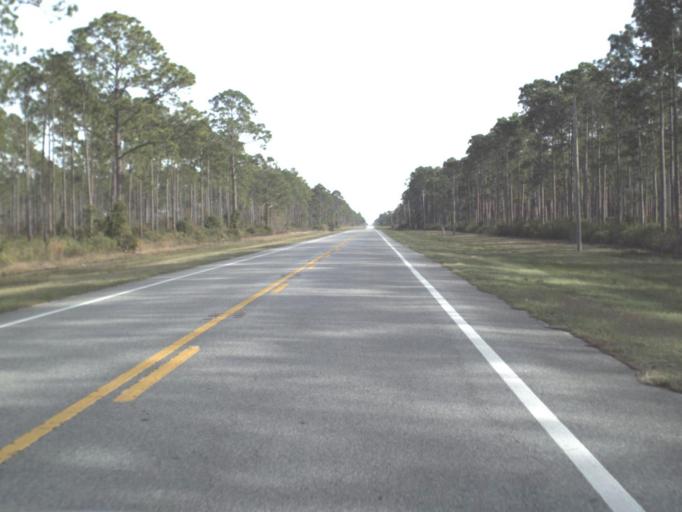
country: US
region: Florida
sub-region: Bay County
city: Tyndall Air Force Base
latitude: 30.0498
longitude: -85.5640
